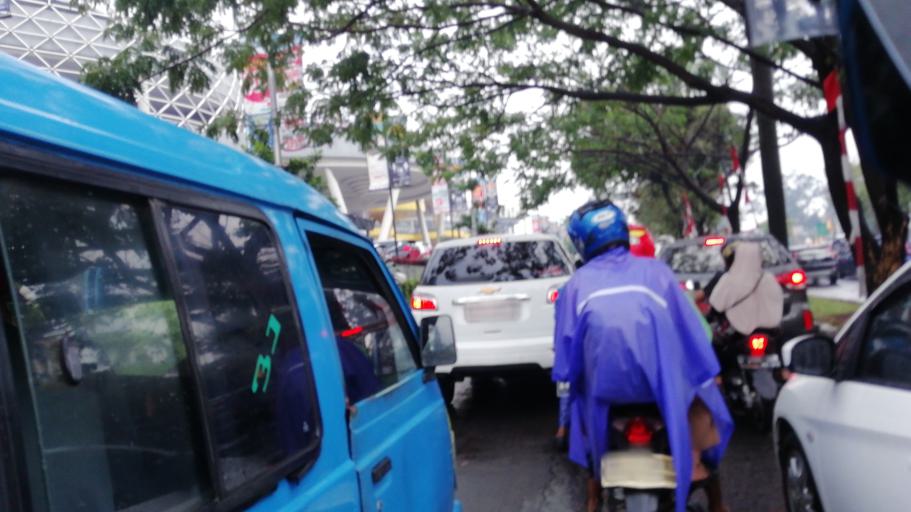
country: ID
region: West Java
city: Cibinong
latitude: -6.4848
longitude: 106.8419
